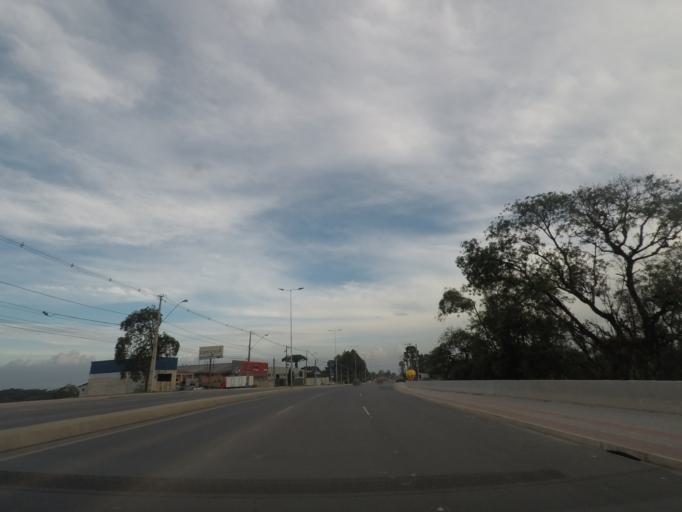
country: BR
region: Parana
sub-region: Colombo
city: Colombo
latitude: -25.3004
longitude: -49.2229
